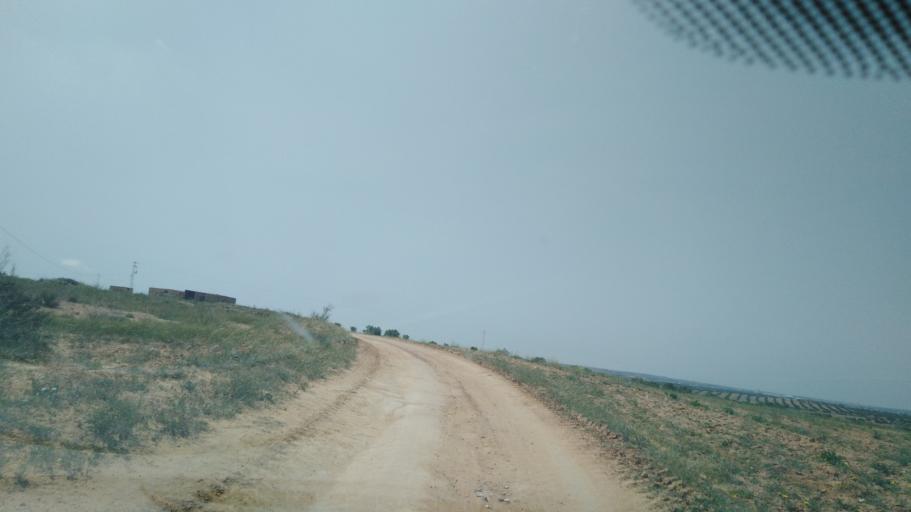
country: TN
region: Safaqis
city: Sfax
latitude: 34.7700
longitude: 10.5783
